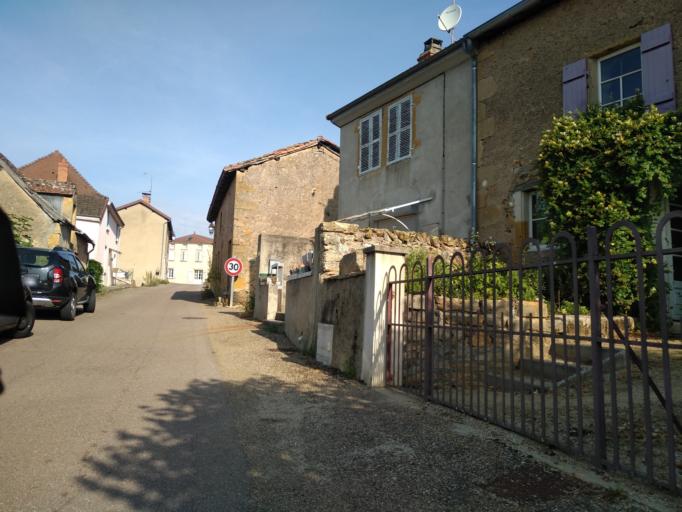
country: FR
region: Bourgogne
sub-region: Departement de Saone-et-Loire
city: Marcigny
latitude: 46.2622
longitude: 4.0923
